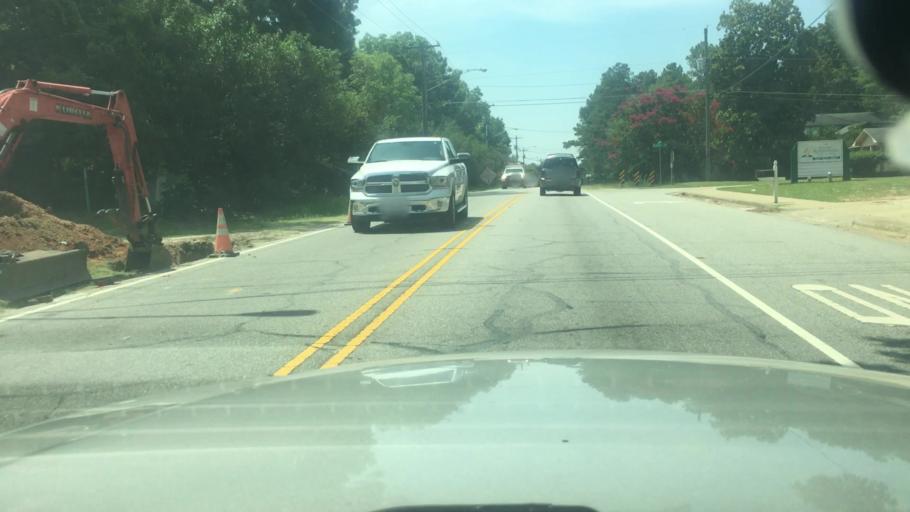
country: US
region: North Carolina
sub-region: Hoke County
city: Rockfish
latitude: 35.0385
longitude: -78.9973
